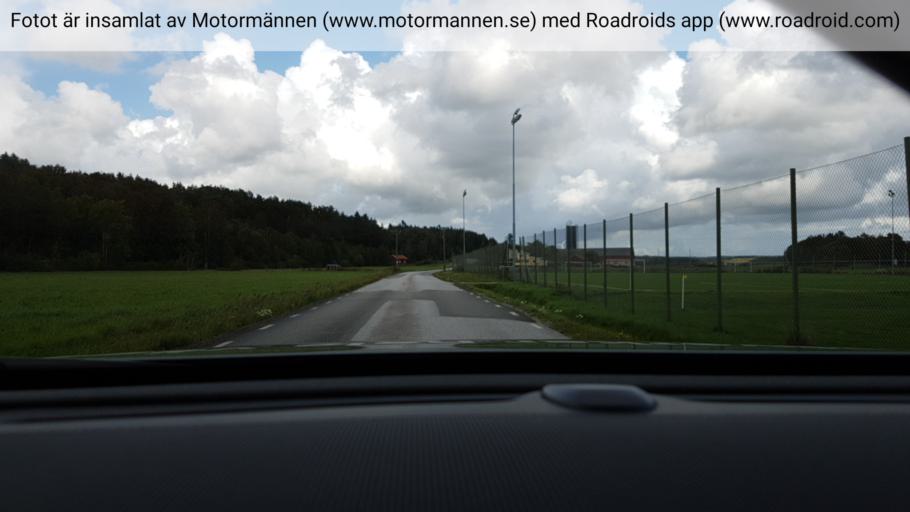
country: SE
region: Vaestra Goetaland
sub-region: Orust
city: Henan
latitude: 58.1428
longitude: 11.5715
